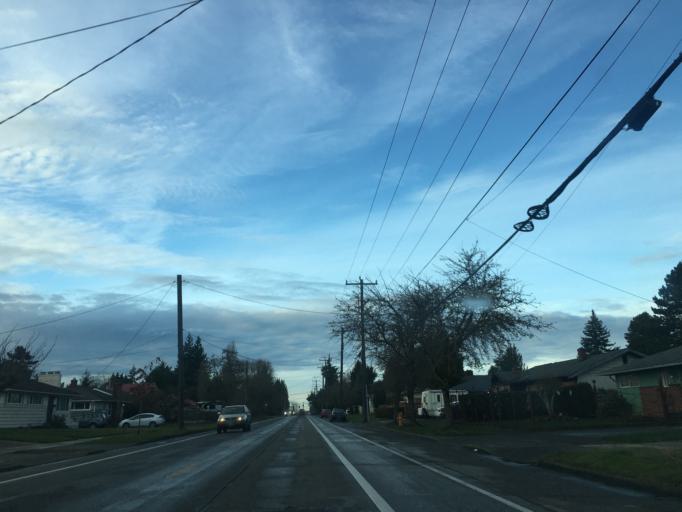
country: US
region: Washington
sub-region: King County
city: Bryn Mawr-Skyway
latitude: 47.5040
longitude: -122.2521
